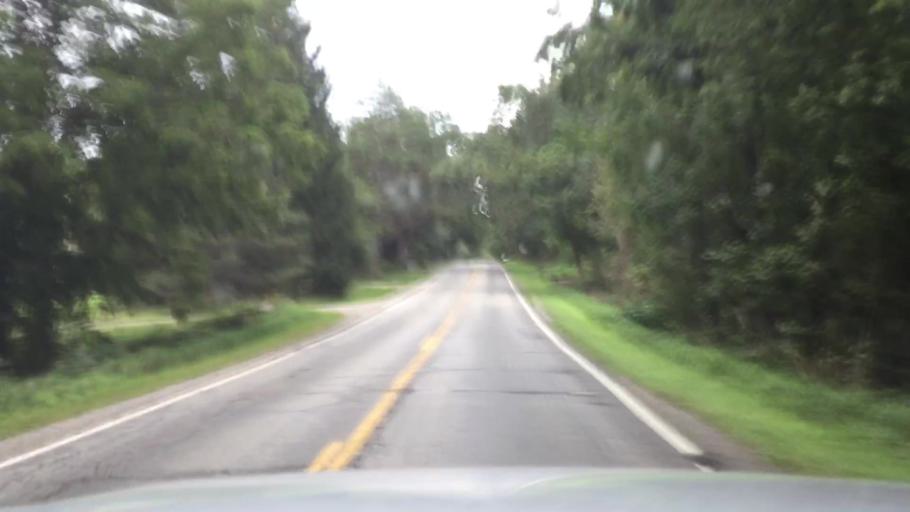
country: US
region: Michigan
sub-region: Genesee County
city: Argentine
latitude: 42.8133
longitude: -83.9039
